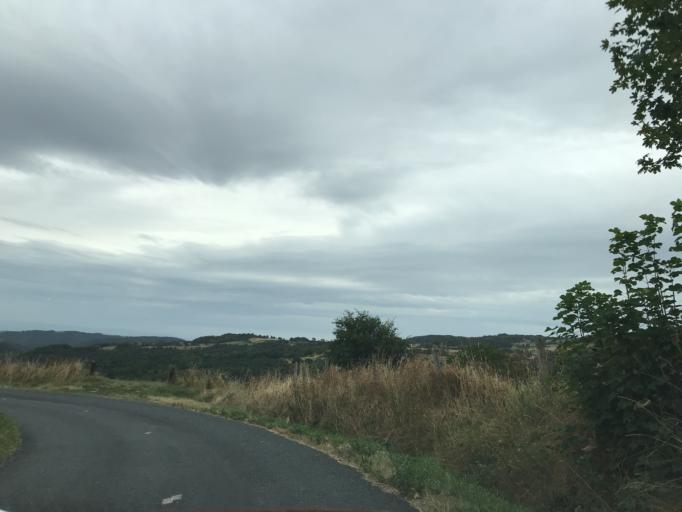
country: FR
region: Rhone-Alpes
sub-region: Departement de la Loire
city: Sail-sous-Couzan
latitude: 45.6809
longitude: 3.9077
